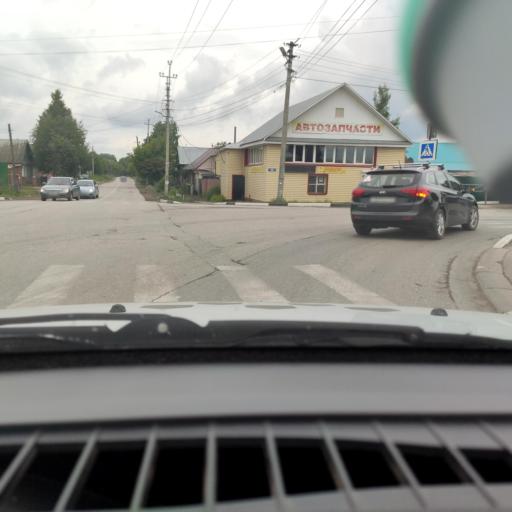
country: RU
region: Perm
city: Kungur
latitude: 57.4403
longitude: 56.9509
